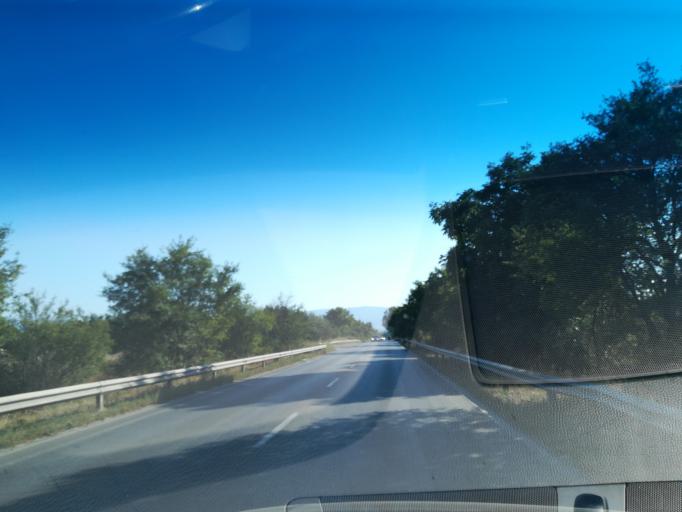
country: BG
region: Plovdiv
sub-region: Obshtina Plovdiv
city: Plovdiv
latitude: 42.1691
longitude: 24.8175
